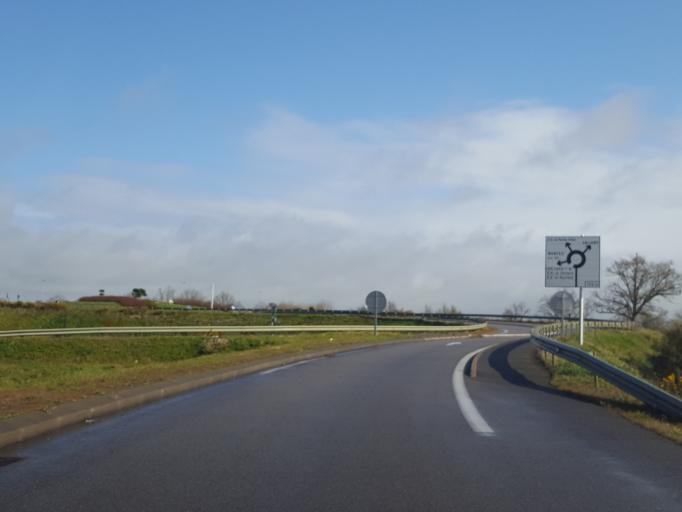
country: FR
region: Pays de la Loire
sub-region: Departement de la Vendee
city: Saligny
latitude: 46.7967
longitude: -1.4292
